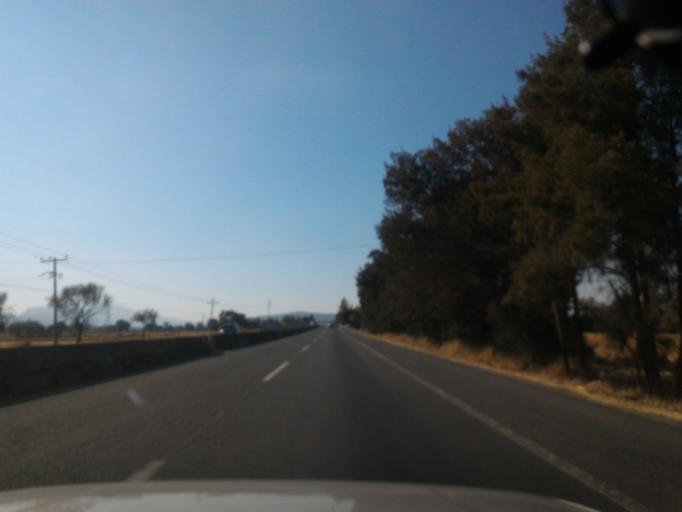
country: MX
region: Jalisco
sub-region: Ixtlahuacan de los Membrillos
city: Valle de los Girasoles [Fraccionamiento]
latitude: 20.4065
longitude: -103.1901
